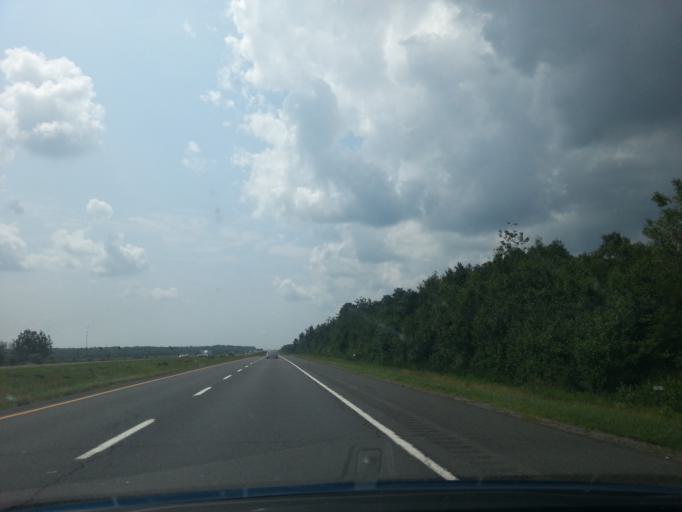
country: CA
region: Quebec
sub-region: Chaudiere-Appalaches
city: Saint-Antoine-de-Tilly
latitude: 46.5932
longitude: -71.5442
